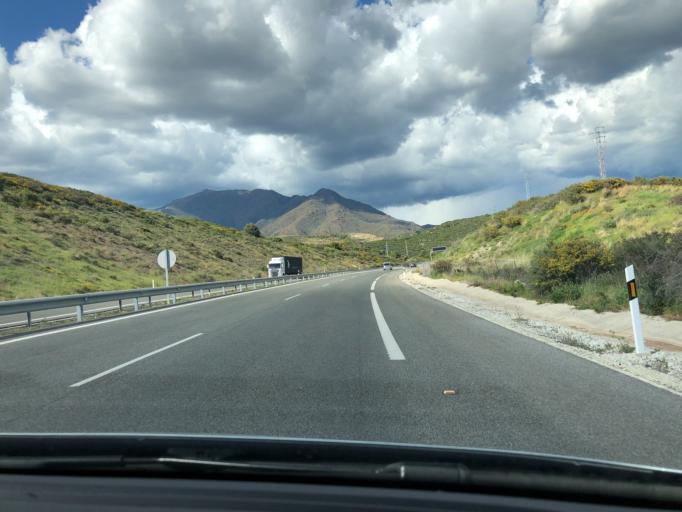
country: ES
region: Andalusia
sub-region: Provincia de Malaga
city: Manilva
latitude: 36.4182
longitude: -5.2201
